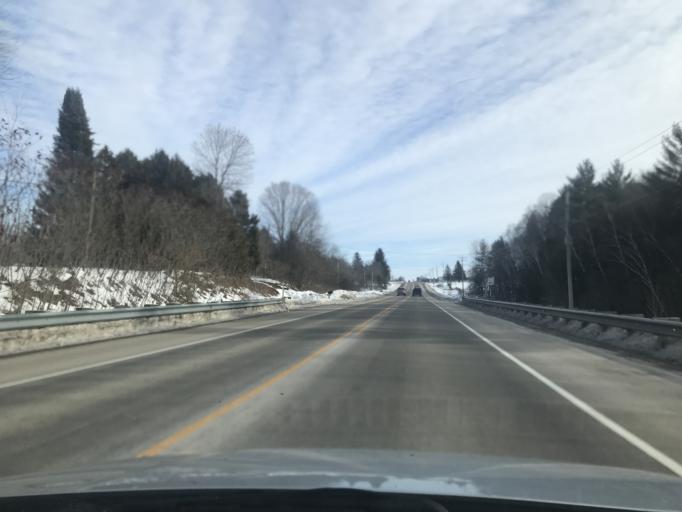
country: US
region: Wisconsin
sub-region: Oconto County
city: Gillett
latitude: 44.8964
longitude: -88.2847
